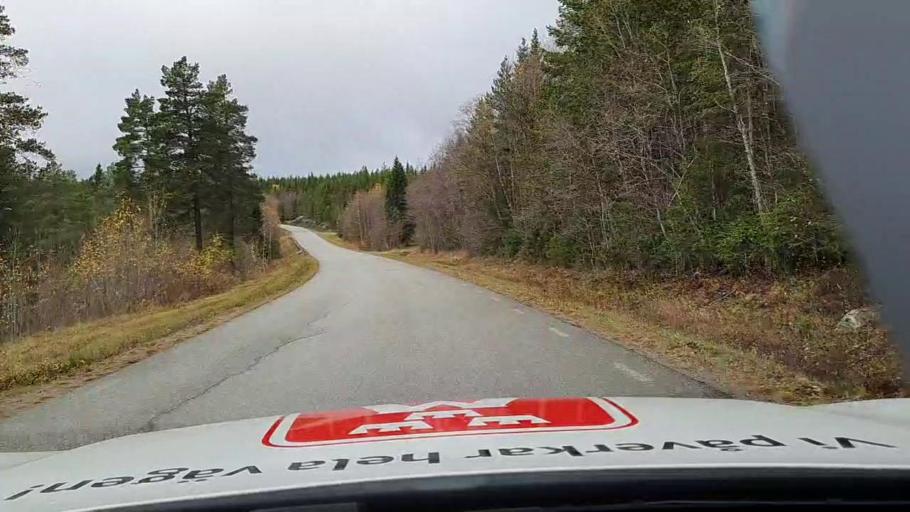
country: SE
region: Jaemtland
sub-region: Bergs Kommun
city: Hoverberg
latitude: 63.0376
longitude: 14.0378
